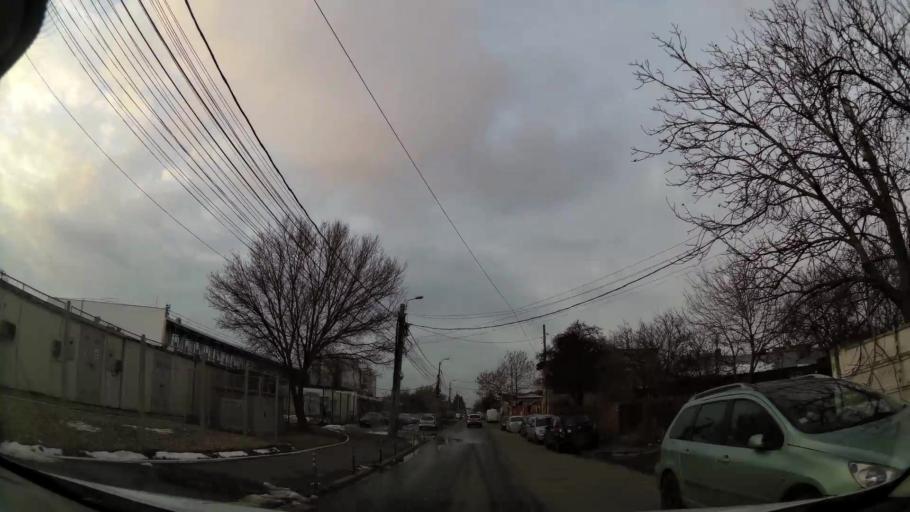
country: RO
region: Ilfov
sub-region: Comuna Fundeni-Dobroesti
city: Fundeni
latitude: 44.4695
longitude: 26.1652
